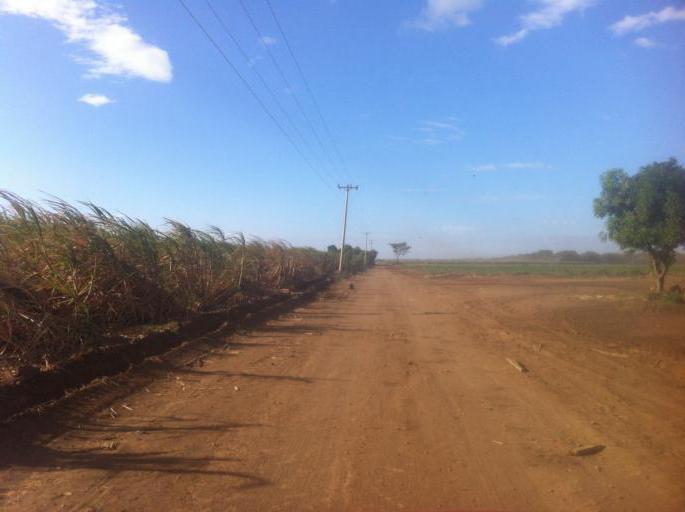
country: NI
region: Managua
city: Masachapa
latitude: 11.8570
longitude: -86.5512
